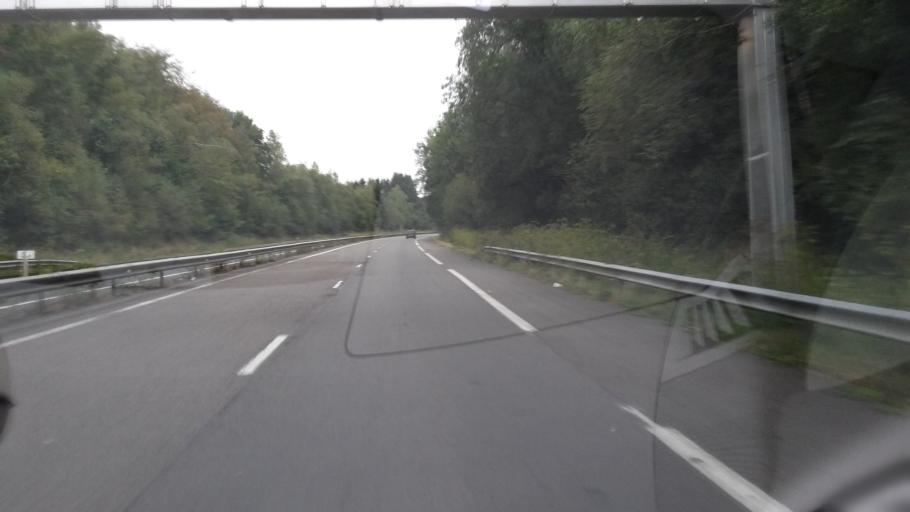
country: BE
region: Wallonia
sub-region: Province du Luxembourg
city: Bouillon
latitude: 49.7430
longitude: 5.0208
